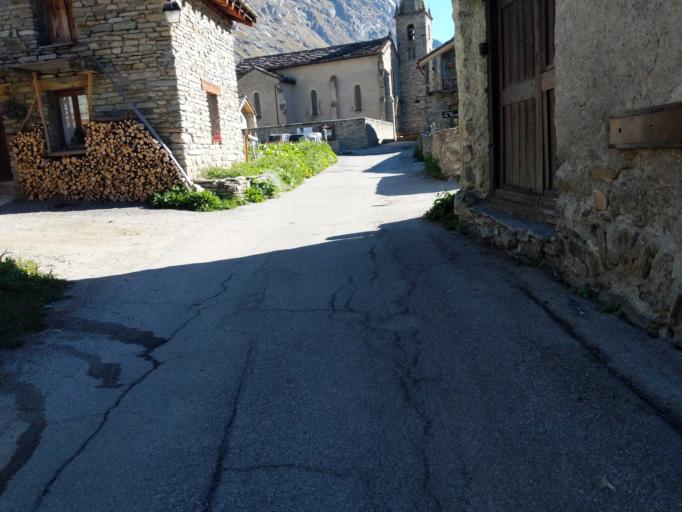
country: FR
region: Rhone-Alpes
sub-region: Departement de la Savoie
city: Val-d'Isere
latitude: 45.3713
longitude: 7.0447
